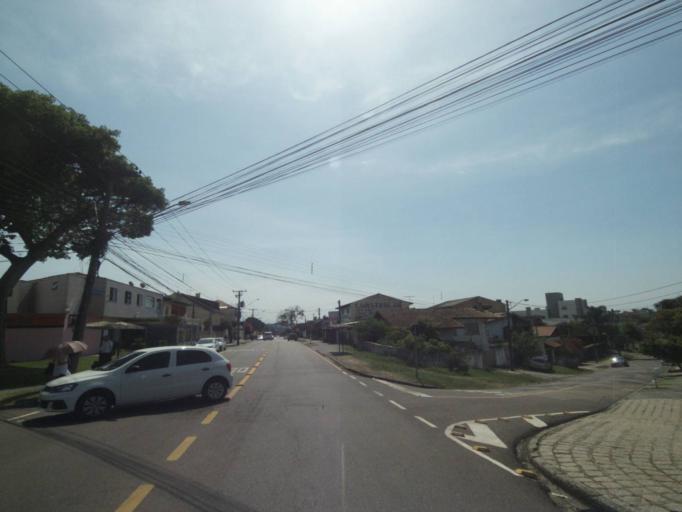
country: BR
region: Parana
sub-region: Curitiba
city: Curitiba
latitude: -25.4708
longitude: -49.3011
